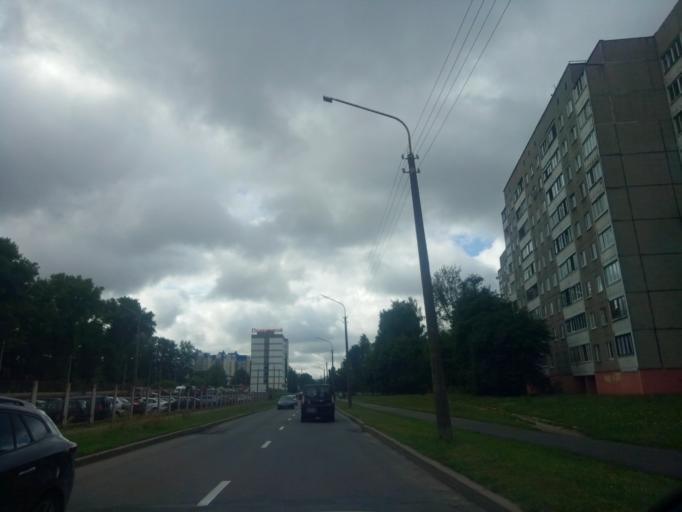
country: BY
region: Minsk
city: Novoye Medvezhino
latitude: 53.9078
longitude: 27.5009
